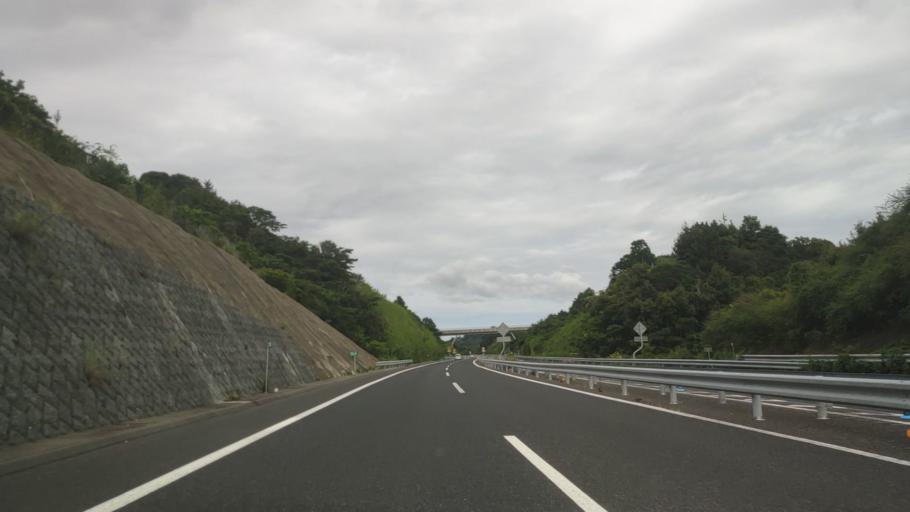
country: JP
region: Wakayama
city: Tanabe
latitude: 33.7594
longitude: 135.3534
